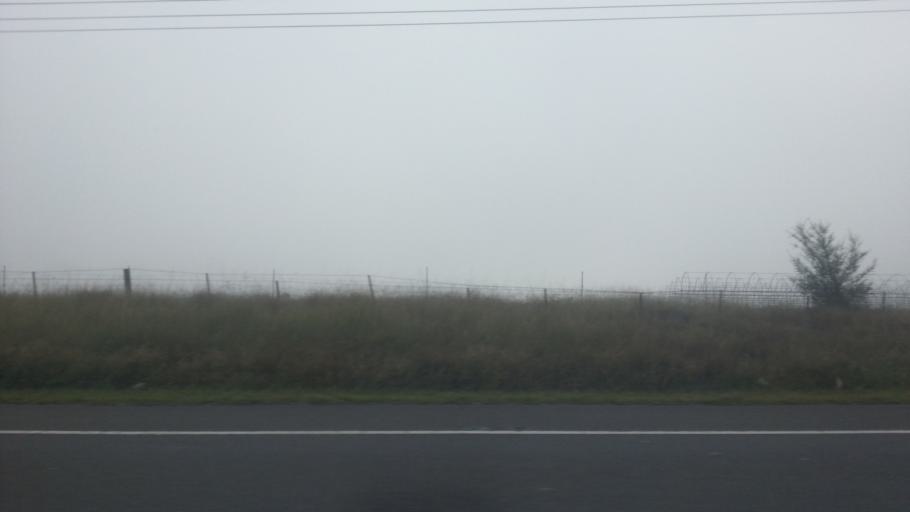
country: AU
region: New South Wales
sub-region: Liverpool
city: Luddenham
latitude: -33.8556
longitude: 150.6942
